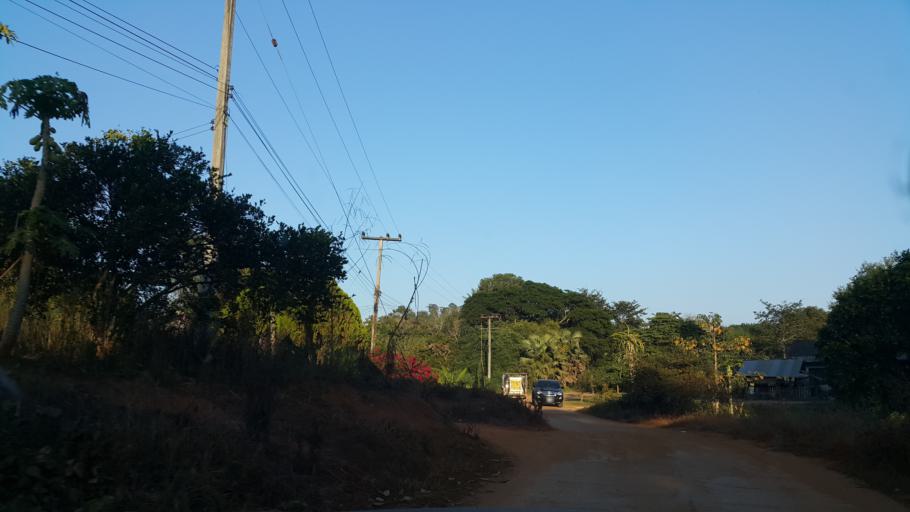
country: TH
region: Sukhothai
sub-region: Amphoe Si Satchanalai
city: Si Satchanalai
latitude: 17.6202
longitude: 99.6259
